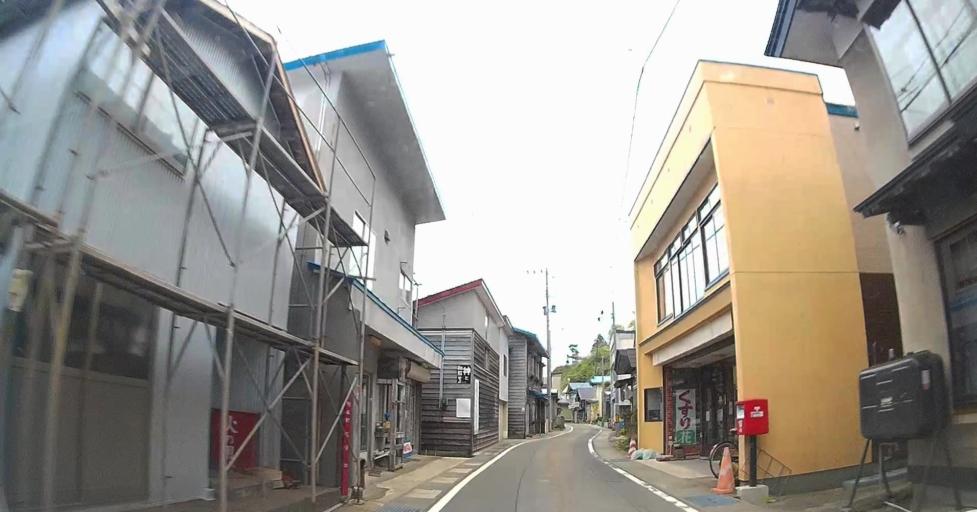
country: JP
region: Aomori
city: Shimokizukuri
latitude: 41.2021
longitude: 140.4288
